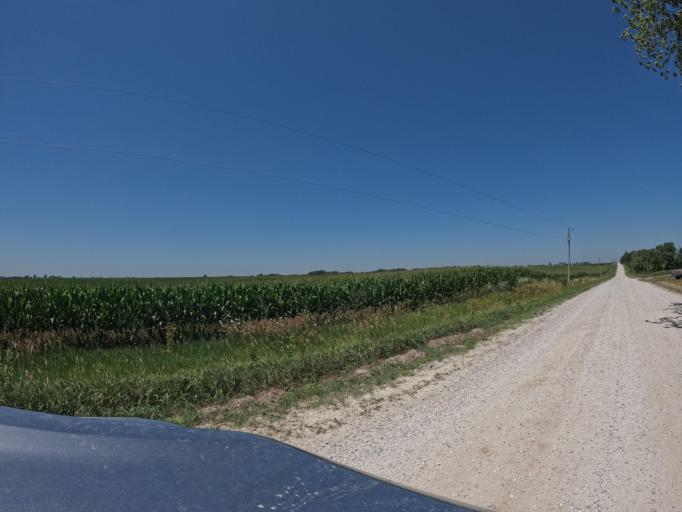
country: US
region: Iowa
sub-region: Keokuk County
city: Sigourney
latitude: 41.4556
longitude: -92.3358
